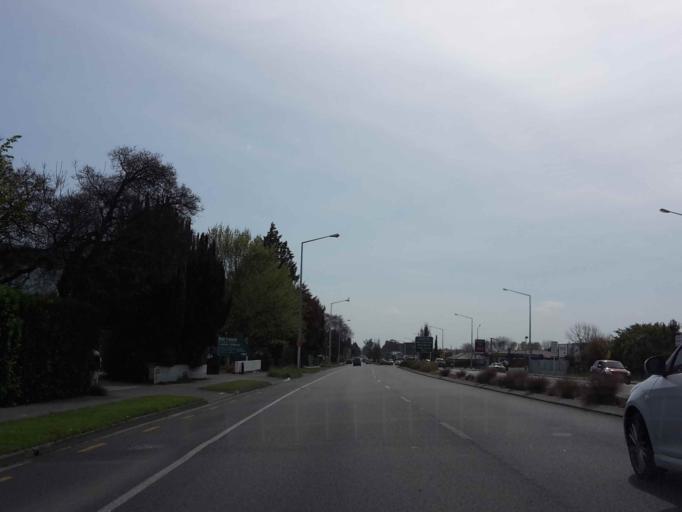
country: NZ
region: Canterbury
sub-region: Waimakariri District
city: Kaiapoi
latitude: -43.4506
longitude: 172.6286
